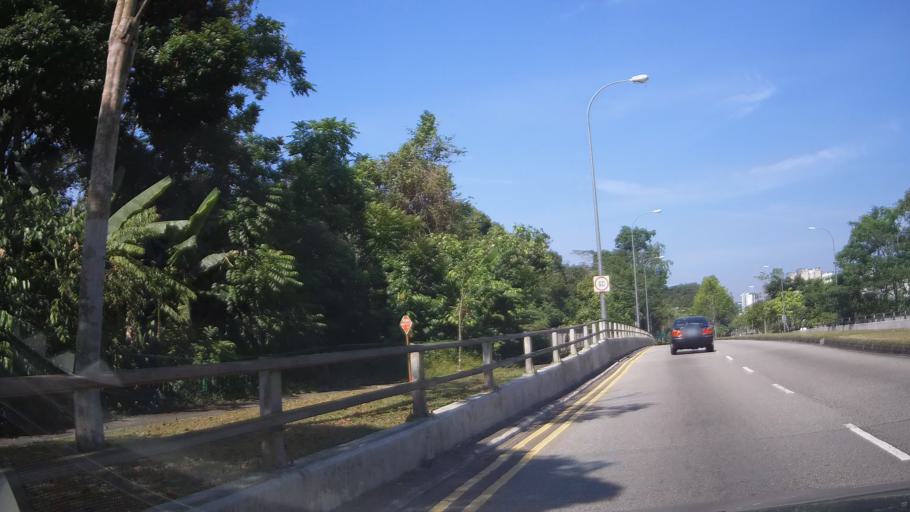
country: MY
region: Johor
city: Johor Bahru
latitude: 1.3652
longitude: 103.7789
